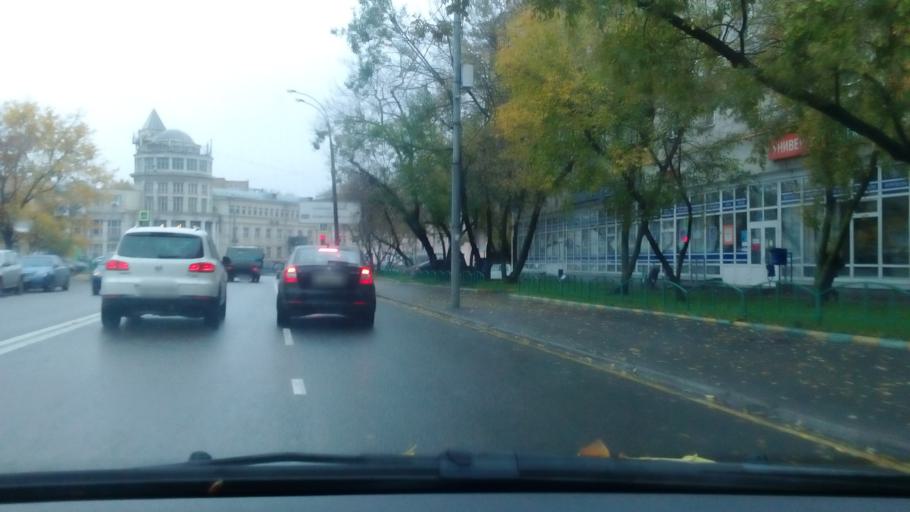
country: RU
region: Moscow
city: Mar'ina Roshcha
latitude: 55.7929
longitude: 37.5771
